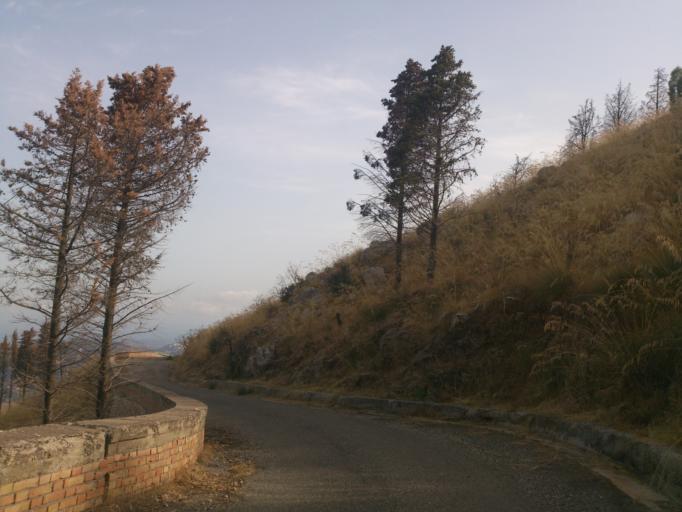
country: IT
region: Calabria
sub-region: Provincia di Reggio Calabria
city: Pazzano
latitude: 38.4706
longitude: 16.4505
